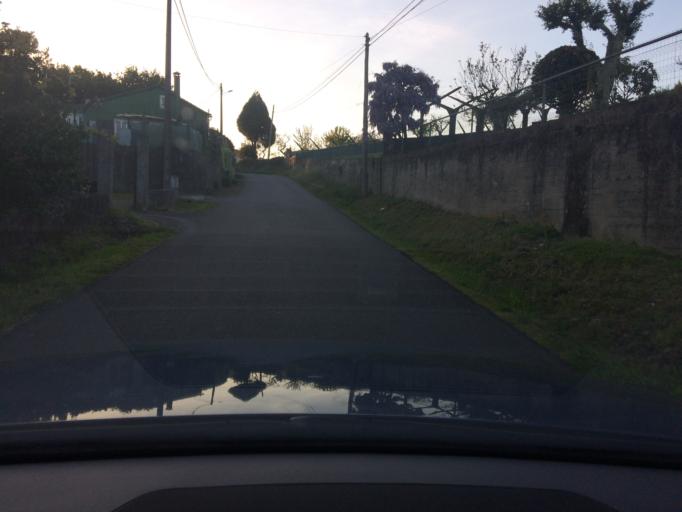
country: ES
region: Galicia
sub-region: Provincia da Coruna
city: Santiago de Compostela
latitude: 42.8328
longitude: -8.5999
